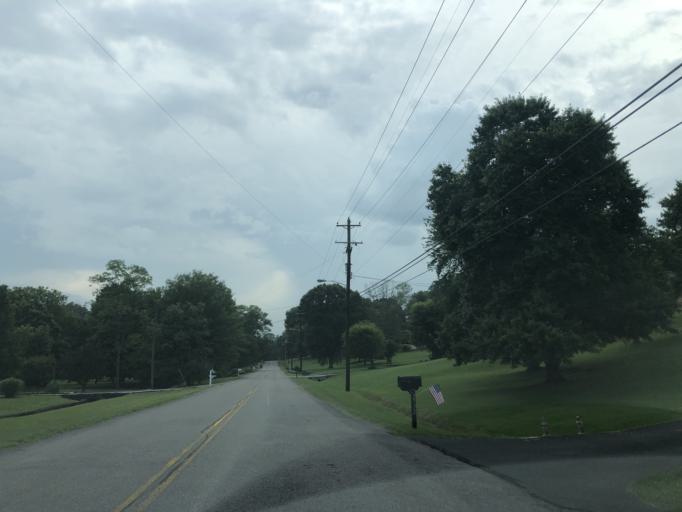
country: US
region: Tennessee
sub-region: Davidson County
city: Lakewood
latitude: 36.1827
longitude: -86.6857
